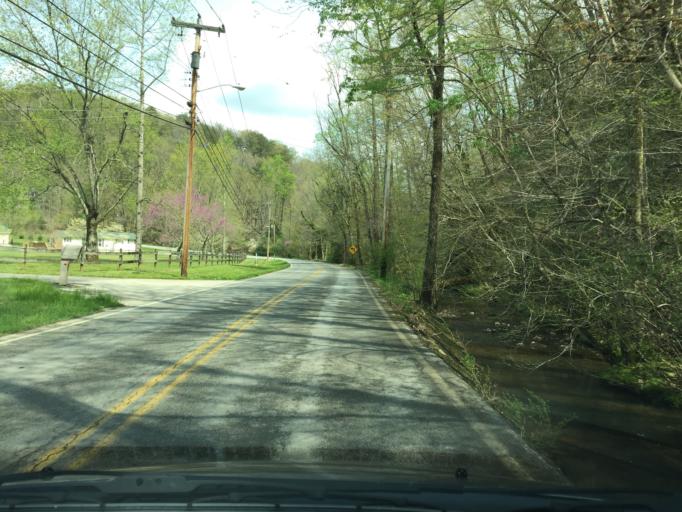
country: US
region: Tennessee
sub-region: Hamilton County
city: Walden
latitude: 35.1624
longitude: -85.2761
